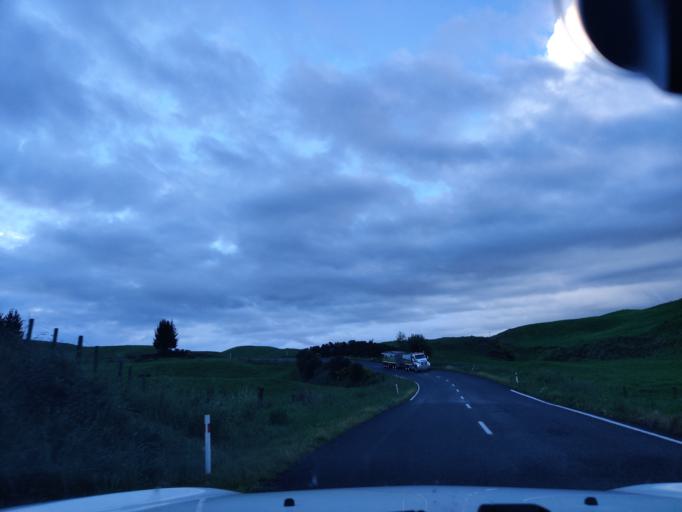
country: NZ
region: Waikato
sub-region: South Waikato District
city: Tokoroa
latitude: -38.2026
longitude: 175.8125
